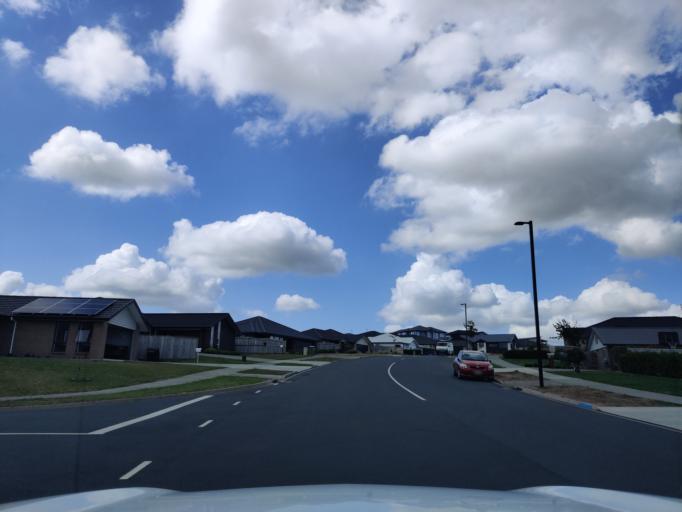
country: NZ
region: Auckland
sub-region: Auckland
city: Pukekohe East
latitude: -37.2369
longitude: 175.0175
